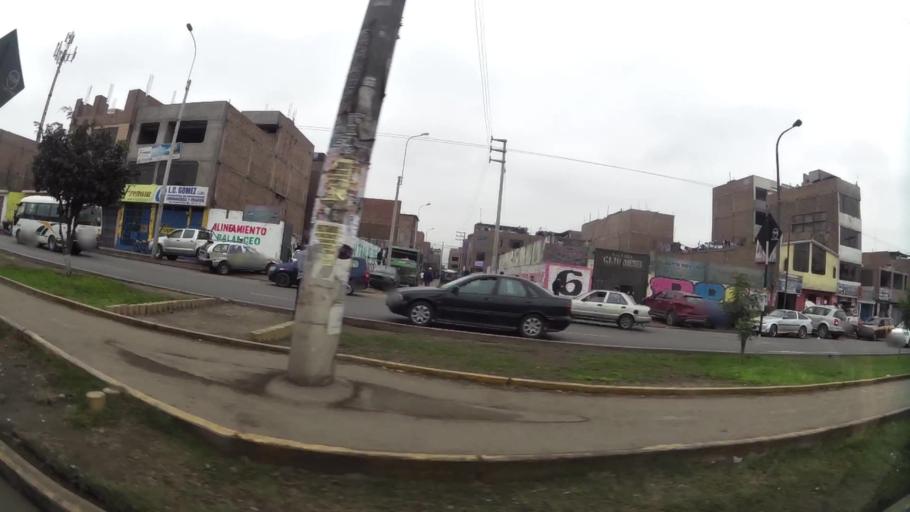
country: PE
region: Lima
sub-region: Lima
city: Vitarte
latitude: -12.0403
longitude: -76.9591
